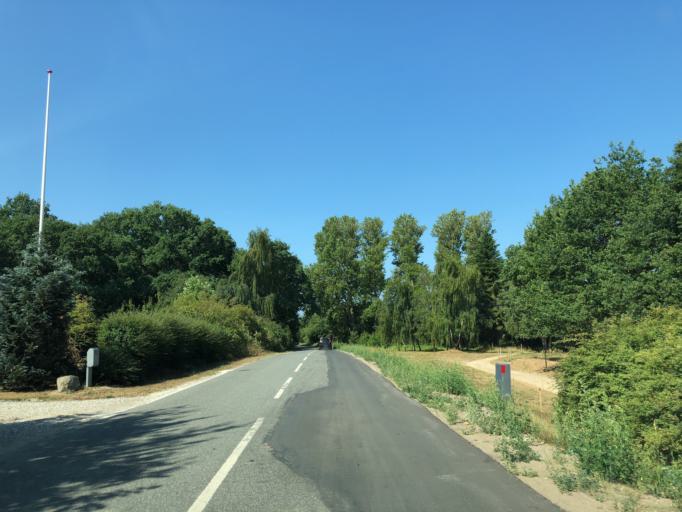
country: DK
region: Capital Region
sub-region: Halsnaes Kommune
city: Hundested
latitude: 55.9746
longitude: 11.8884
